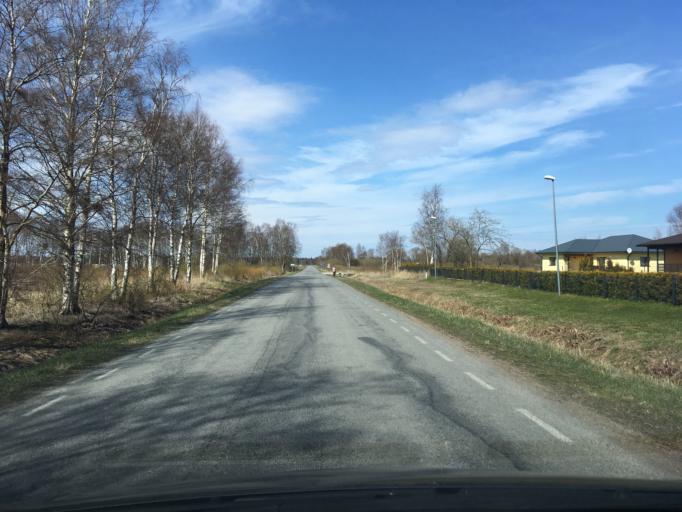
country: EE
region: Harju
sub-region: Raasiku vald
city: Raasiku
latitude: 59.3689
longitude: 25.1734
